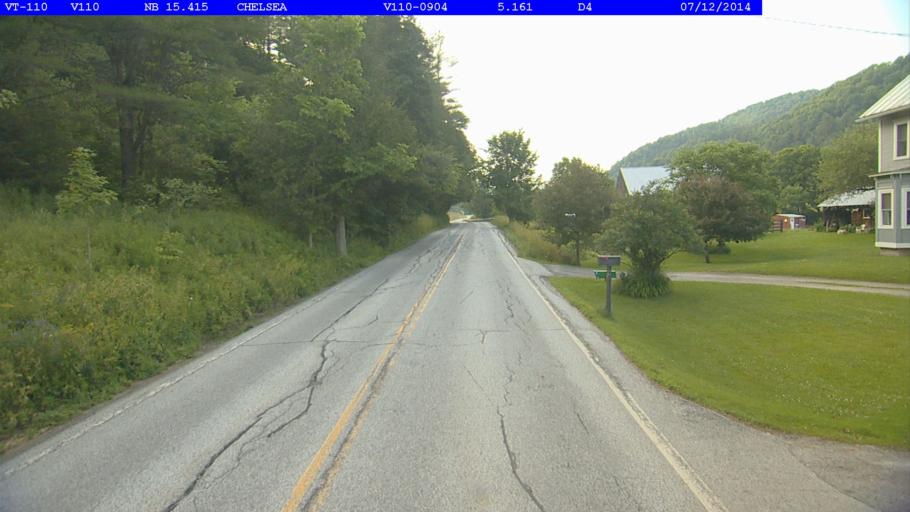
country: US
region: Vermont
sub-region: Orange County
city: Chelsea
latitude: 44.0163
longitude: -72.4649
